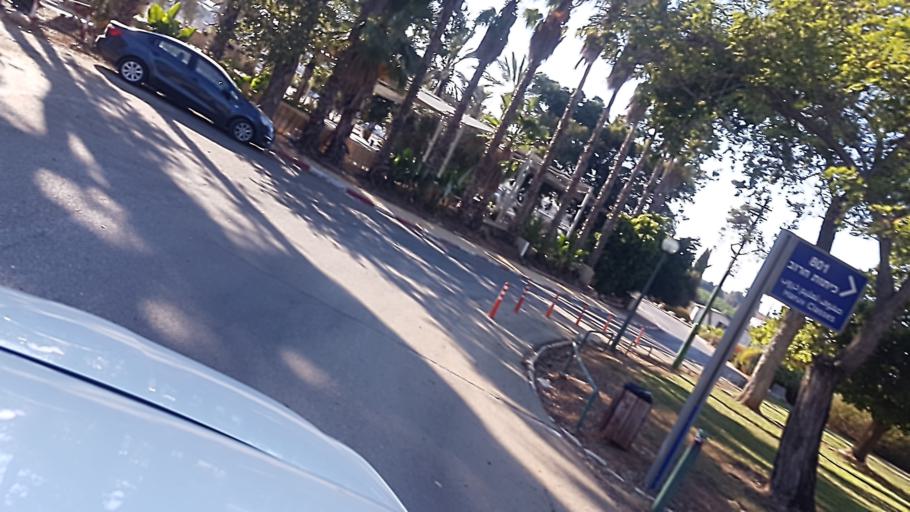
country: IL
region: Central District
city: Kfar Saba
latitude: 32.2008
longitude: 34.9249
